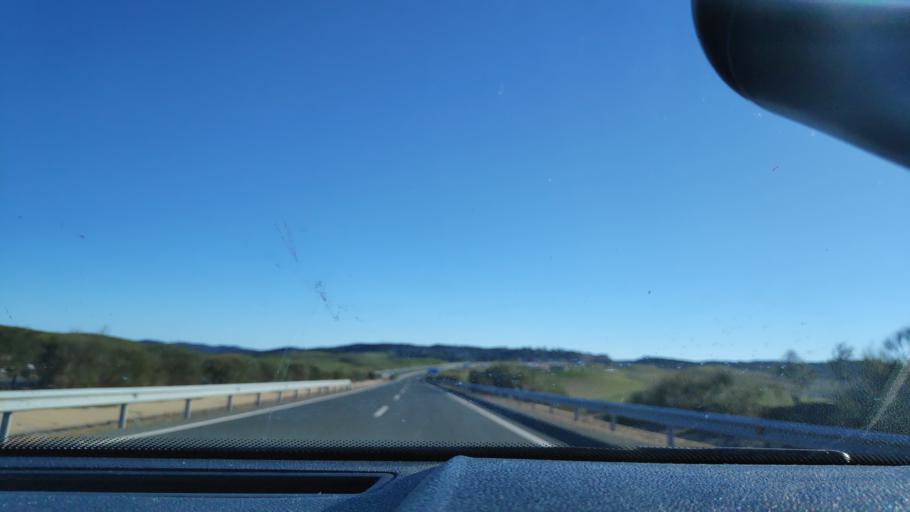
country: ES
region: Extremadura
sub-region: Provincia de Badajoz
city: Monesterio
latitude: 38.1510
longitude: -6.2796
